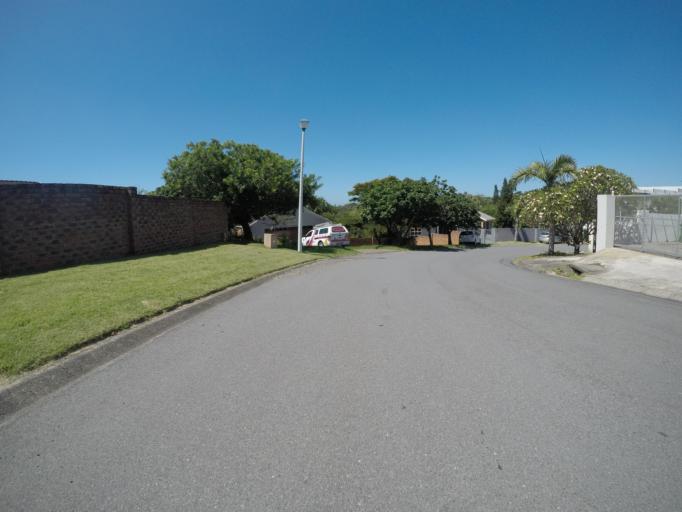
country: ZA
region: Eastern Cape
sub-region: Buffalo City Metropolitan Municipality
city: East London
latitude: -32.9708
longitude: 27.9449
